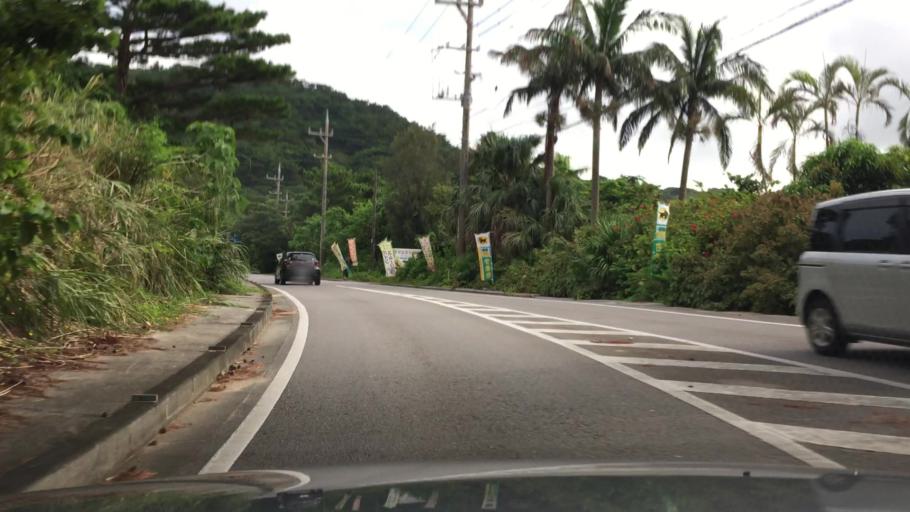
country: JP
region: Okinawa
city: Ishigaki
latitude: 24.4456
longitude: 124.1258
